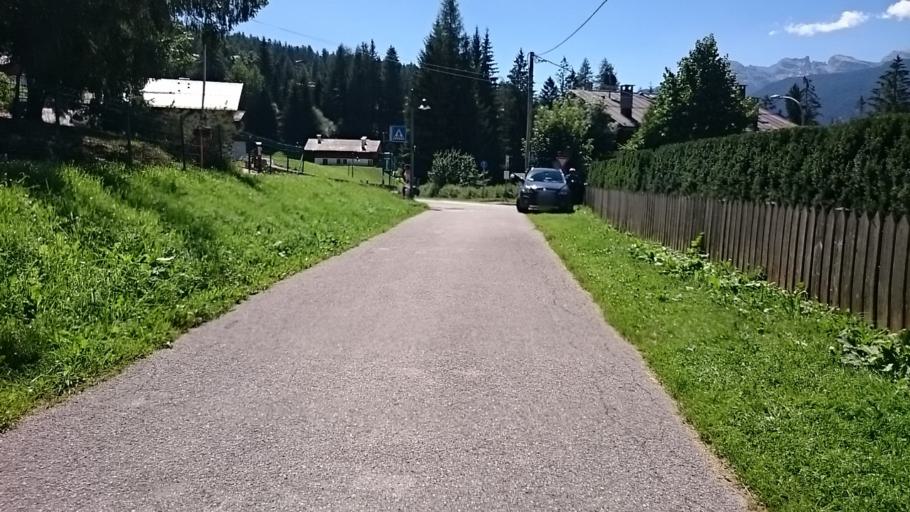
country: IT
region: Veneto
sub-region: Provincia di Belluno
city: Cortina d'Ampezzo
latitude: 46.5356
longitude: 12.1427
